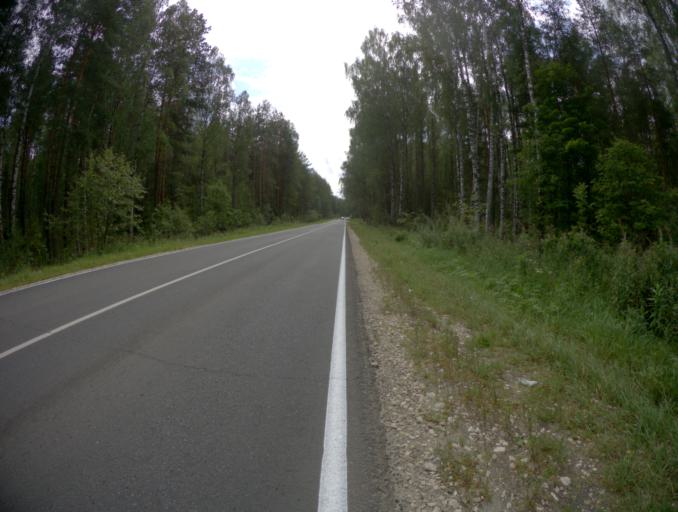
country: RU
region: Vladimir
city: Raduzhnyy
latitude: 55.9981
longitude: 40.2695
